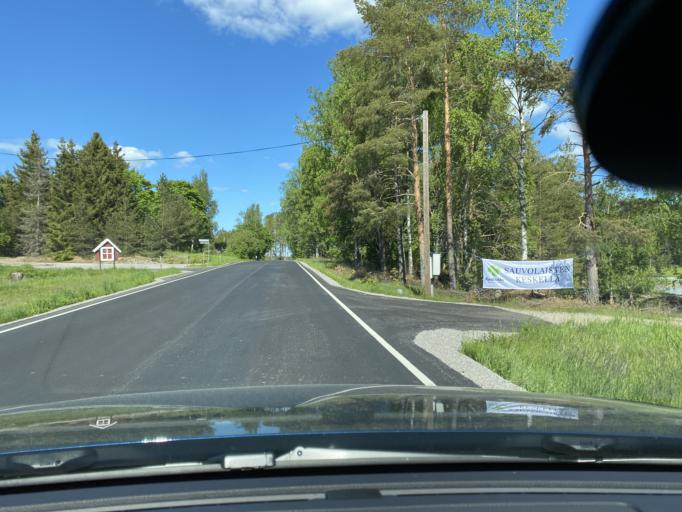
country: FI
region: Varsinais-Suomi
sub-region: Turku
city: Sauvo
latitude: 60.3343
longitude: 22.6843
